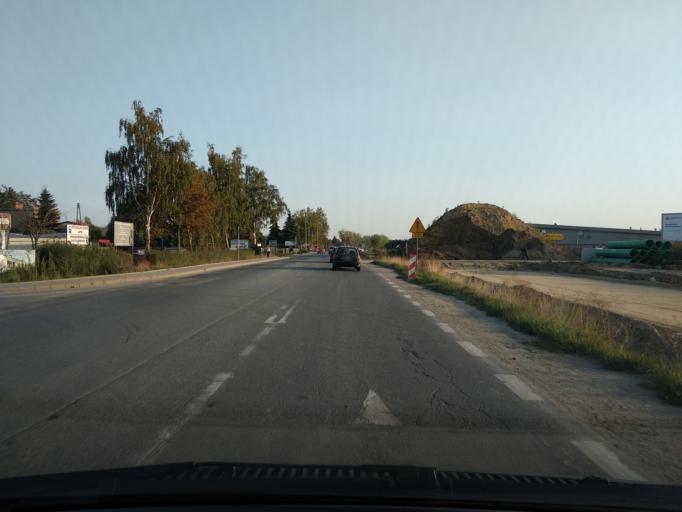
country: PL
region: Lower Silesian Voivodeship
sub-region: Powiat wroclawski
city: Zerniki Wroclawskie
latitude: 51.0516
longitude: 17.0586
